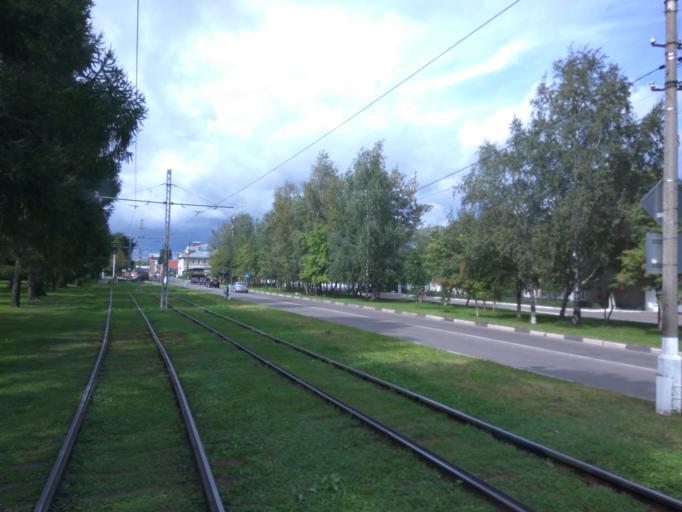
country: RU
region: Moskovskaya
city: Kolomna
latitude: 55.0949
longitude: 38.7727
